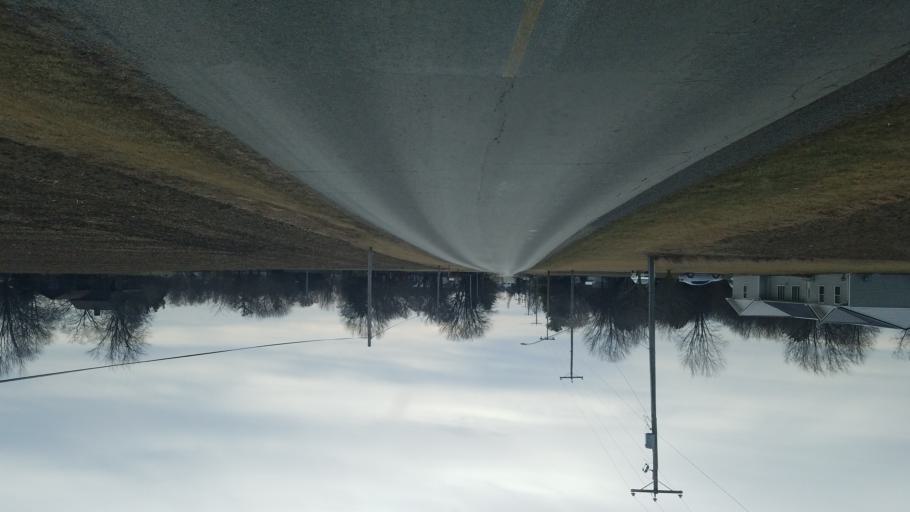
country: US
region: Ohio
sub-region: Hardin County
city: Kenton
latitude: 40.5392
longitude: -83.5159
